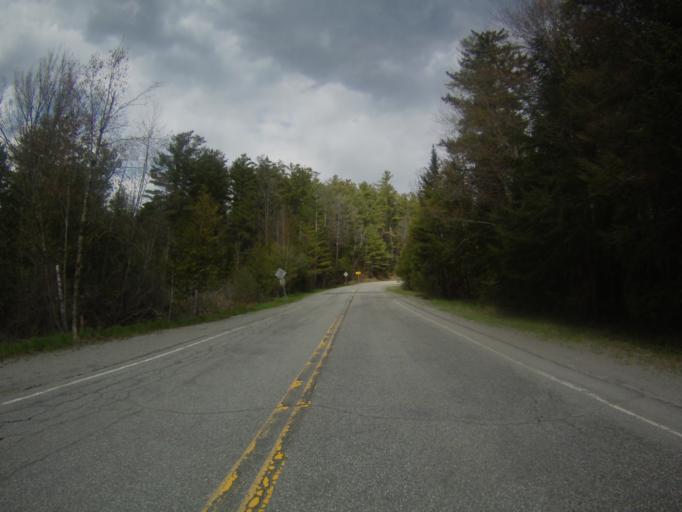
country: US
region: New York
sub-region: Essex County
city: Mineville
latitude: 44.0766
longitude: -73.6586
